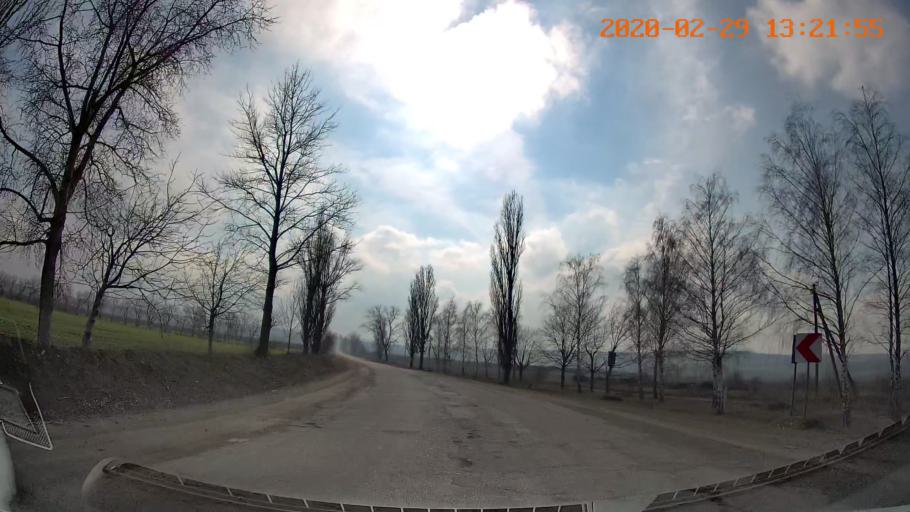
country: MD
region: Telenesti
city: Camenca
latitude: 47.9660
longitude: 28.6290
